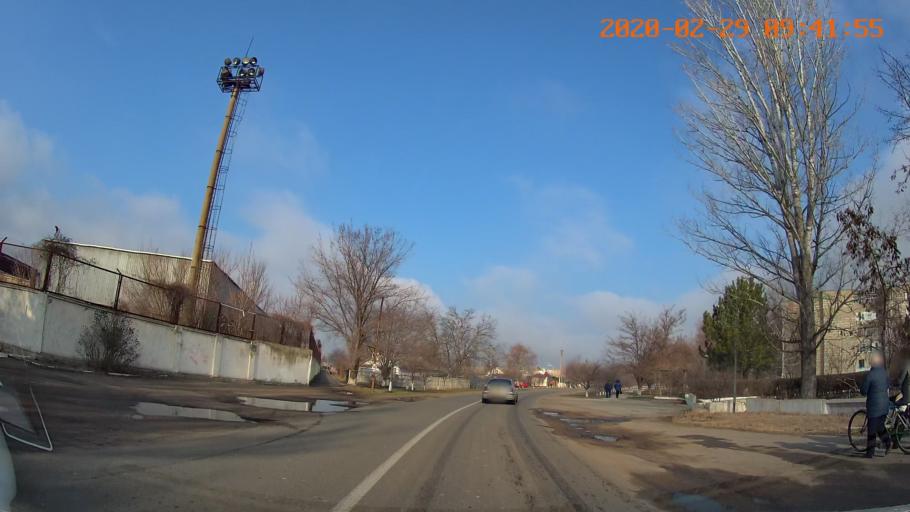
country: MD
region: Telenesti
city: Crasnoe
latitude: 46.6380
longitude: 29.8261
